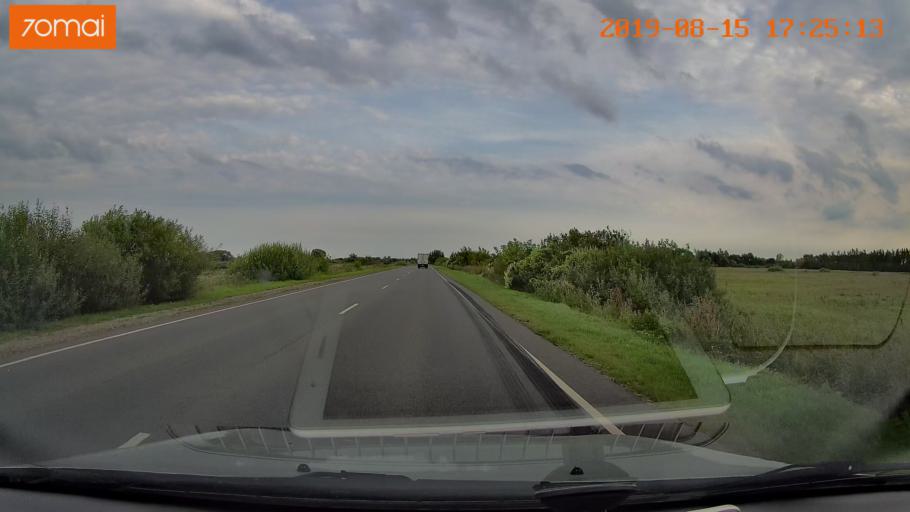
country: RU
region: Moskovskaya
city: Ashitkovo
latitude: 55.3774
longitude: 38.5632
